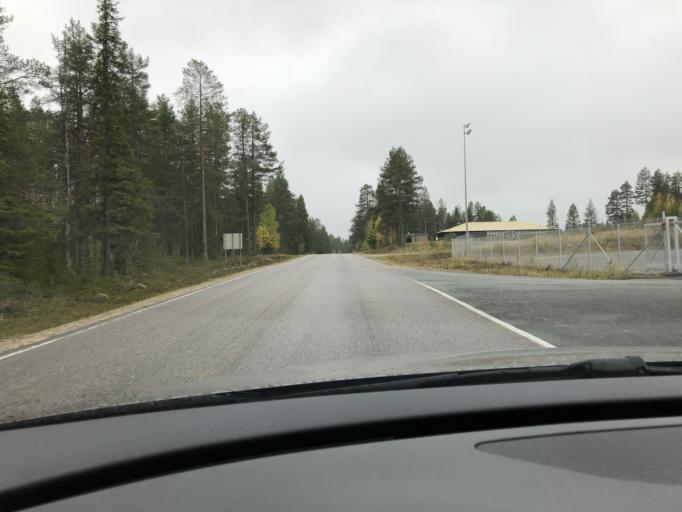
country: FI
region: Lapland
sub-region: Itae-Lappi
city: Posio
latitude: 66.1182
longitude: 28.1824
